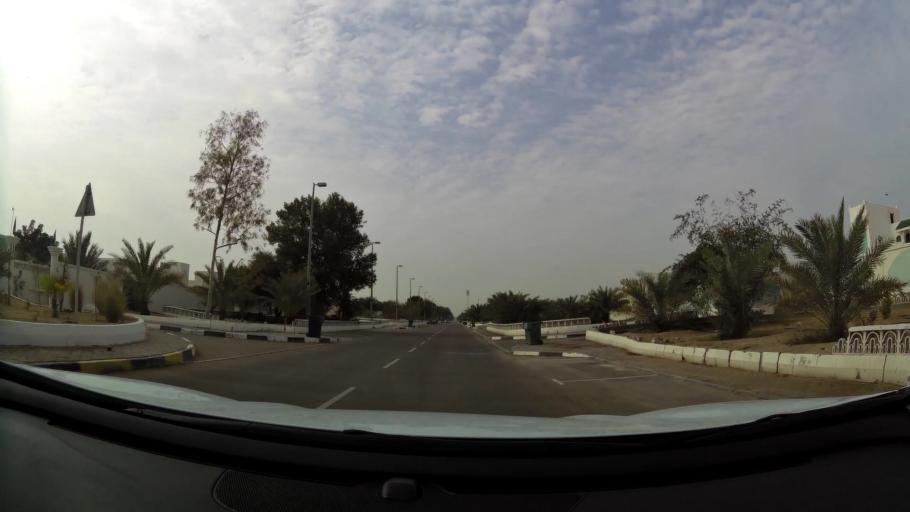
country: AE
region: Abu Dhabi
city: Abu Dhabi
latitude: 24.6794
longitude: 54.7604
